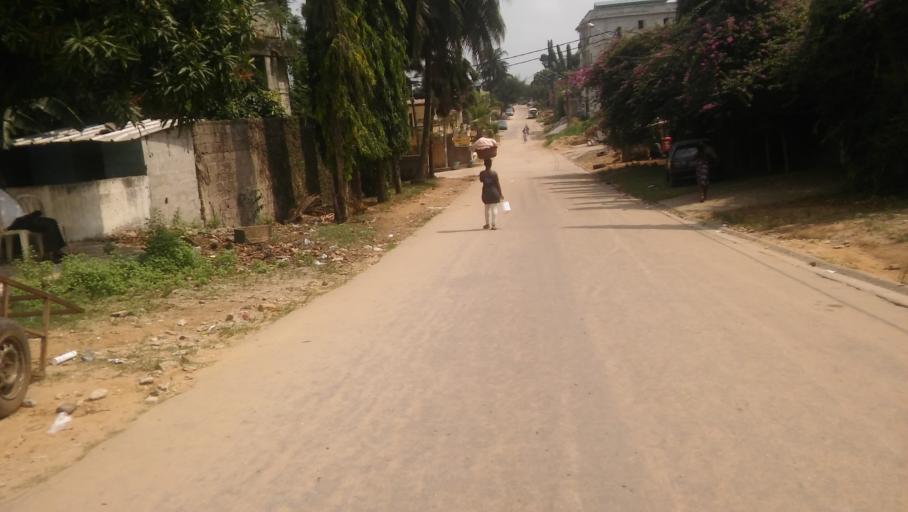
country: CI
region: Lagunes
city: Abidjan
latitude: 5.3582
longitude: -3.9771
